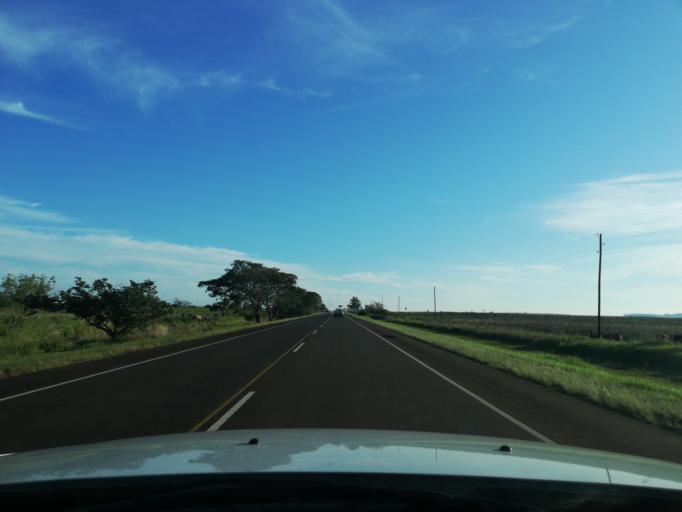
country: AR
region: Misiones
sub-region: Departamento de Capital
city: Posadas
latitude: -27.4428
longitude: -56.0274
